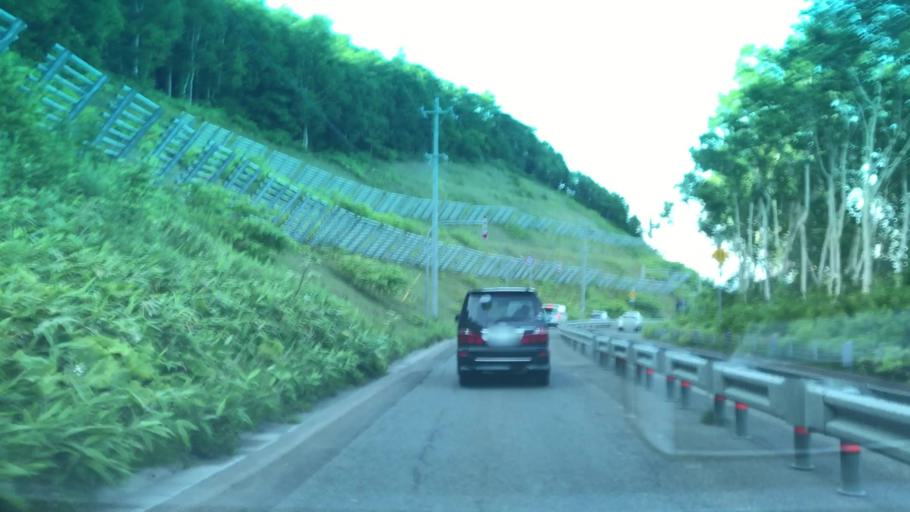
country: JP
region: Hokkaido
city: Otaru
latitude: 43.1379
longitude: 141.0138
